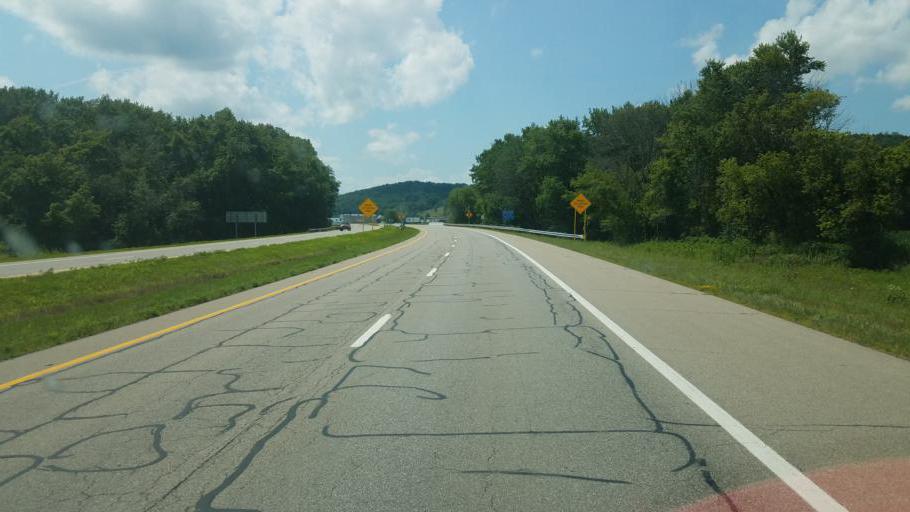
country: US
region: Ohio
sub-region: Coshocton County
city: West Lafayette
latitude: 40.2934
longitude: -81.7447
